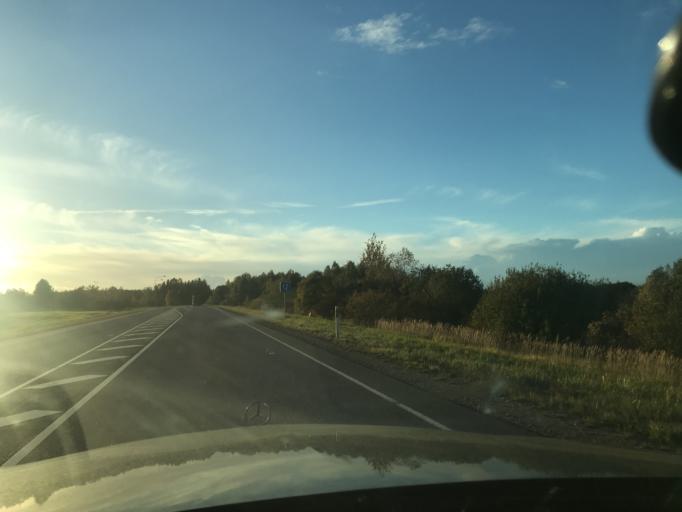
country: EE
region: Vorumaa
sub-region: Voru linn
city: Voru
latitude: 57.8605
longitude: 26.9912
